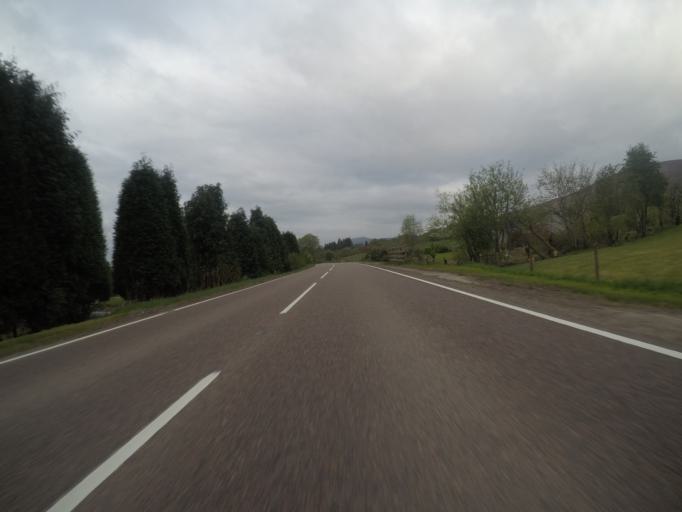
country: GB
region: Scotland
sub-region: Highland
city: Spean Bridge
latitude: 56.8905
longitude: -4.8681
